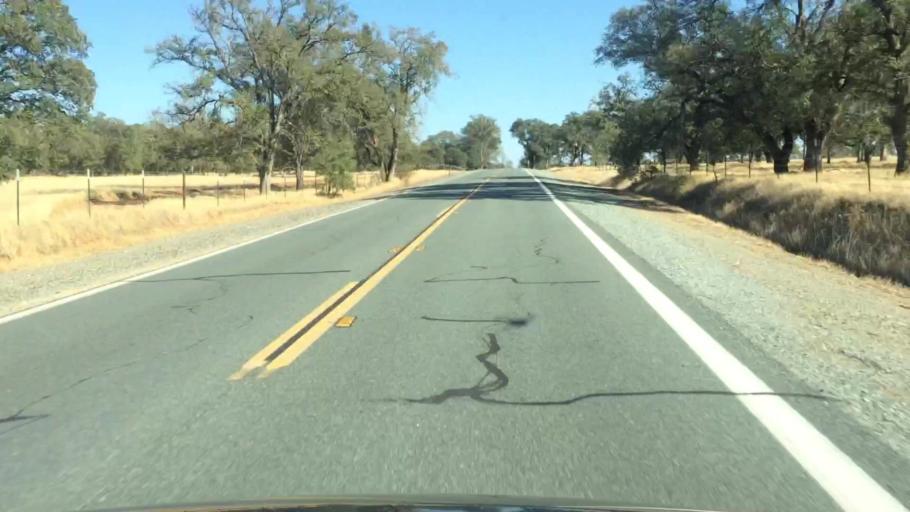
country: US
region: California
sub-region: Amador County
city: Ione
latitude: 38.3824
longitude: -120.9952
